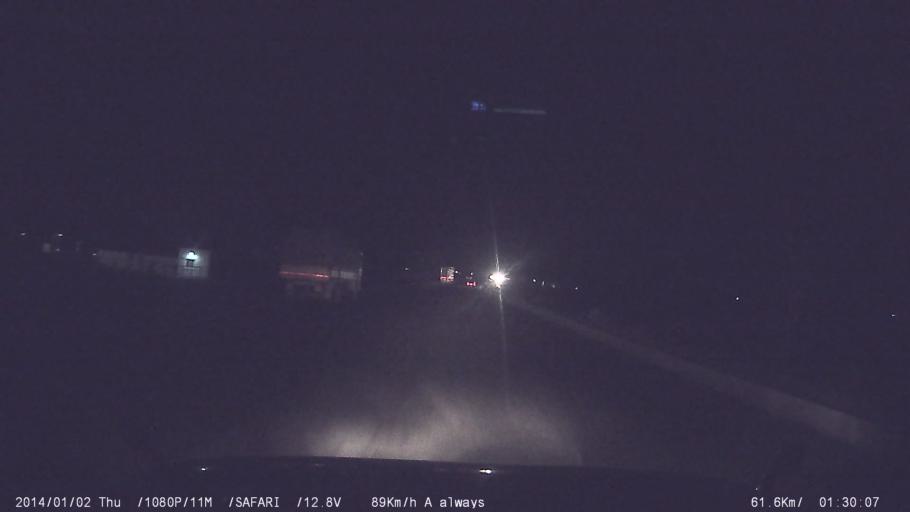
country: IN
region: Tamil Nadu
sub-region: Coimbatore
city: Sulur
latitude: 11.0891
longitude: 77.1331
